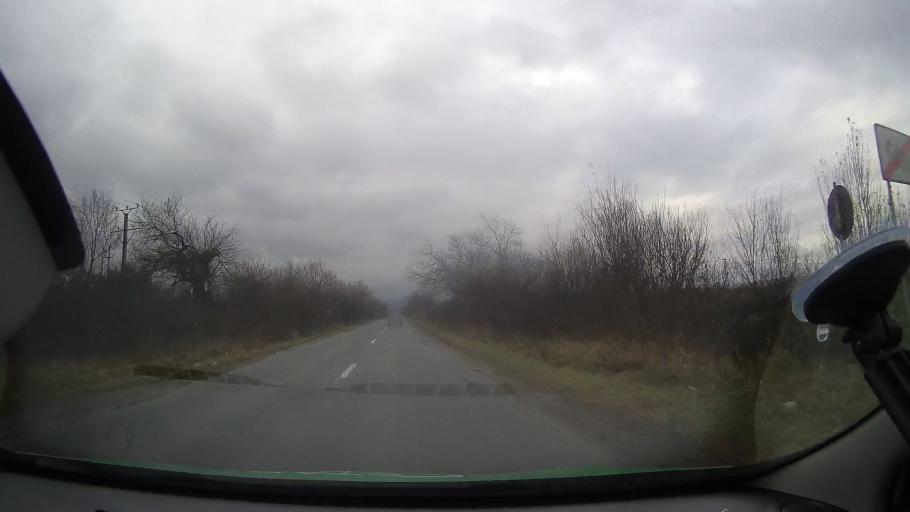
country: RO
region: Arad
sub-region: Comuna Sebis
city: Sebis
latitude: 46.3590
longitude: 22.1306
